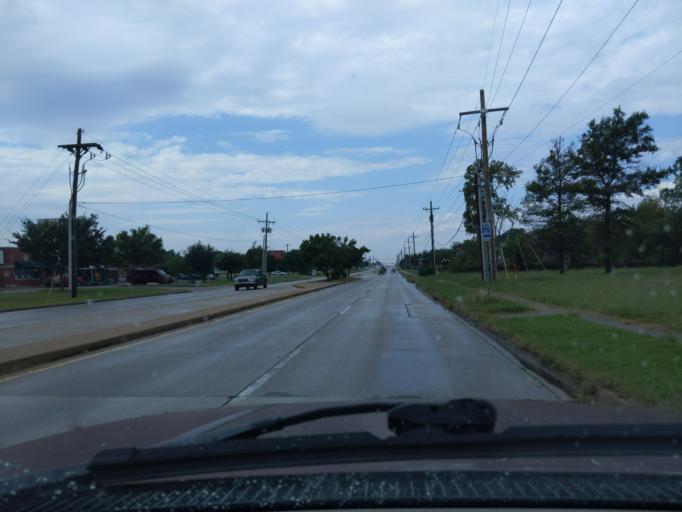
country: US
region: Oklahoma
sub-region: Tulsa County
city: Tulsa
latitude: 36.1336
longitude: -95.8780
